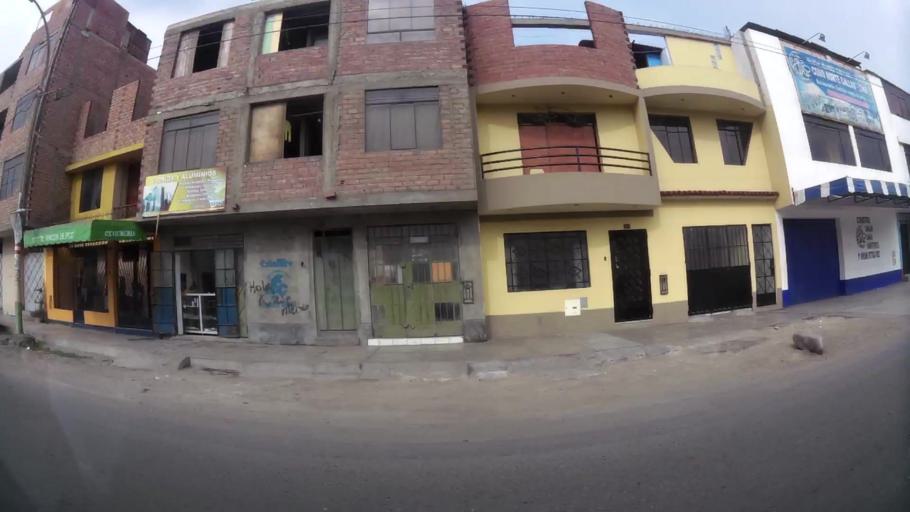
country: PE
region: Callao
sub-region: Callao
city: Callao
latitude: -12.0260
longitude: -77.0936
